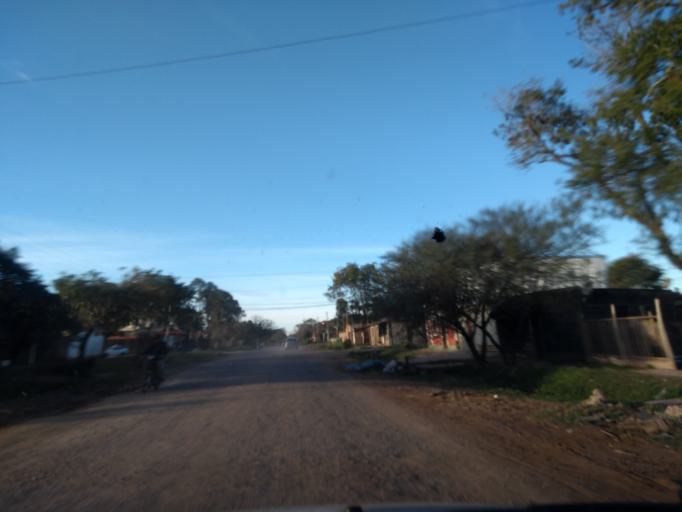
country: AR
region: Chaco
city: Resistencia
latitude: -27.4929
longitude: -58.9759
